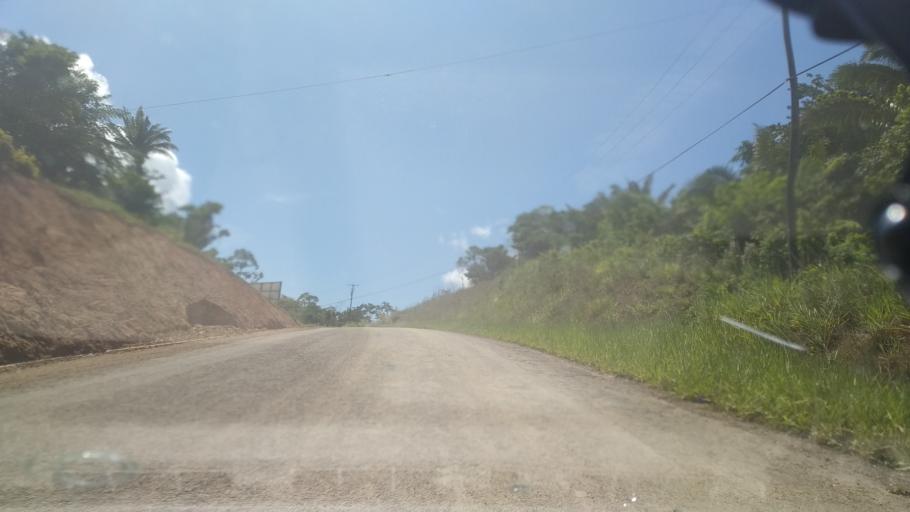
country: BZ
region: Cayo
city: Belmopan
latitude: 17.0497
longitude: -88.5558
